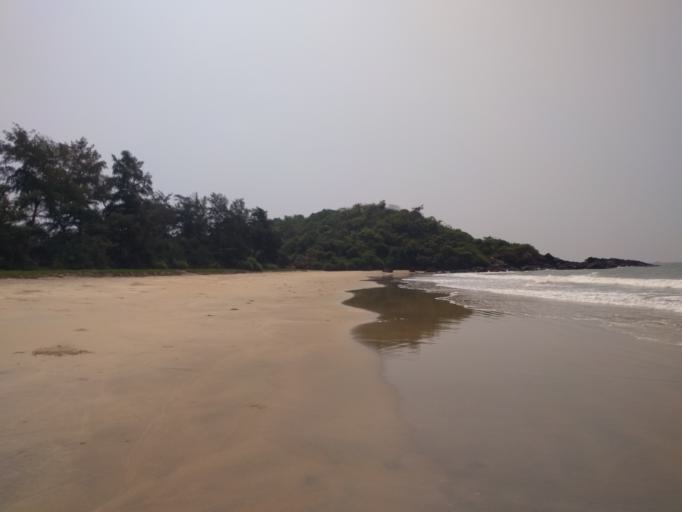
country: IN
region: Karnataka
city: Canacona
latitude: 14.9753
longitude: 74.0430
